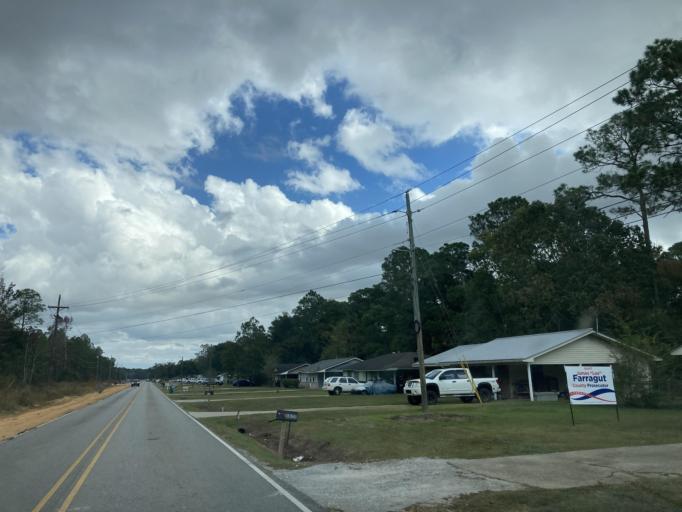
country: US
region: Mississippi
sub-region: Jackson County
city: Gulf Hills
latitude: 30.4390
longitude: -88.8253
